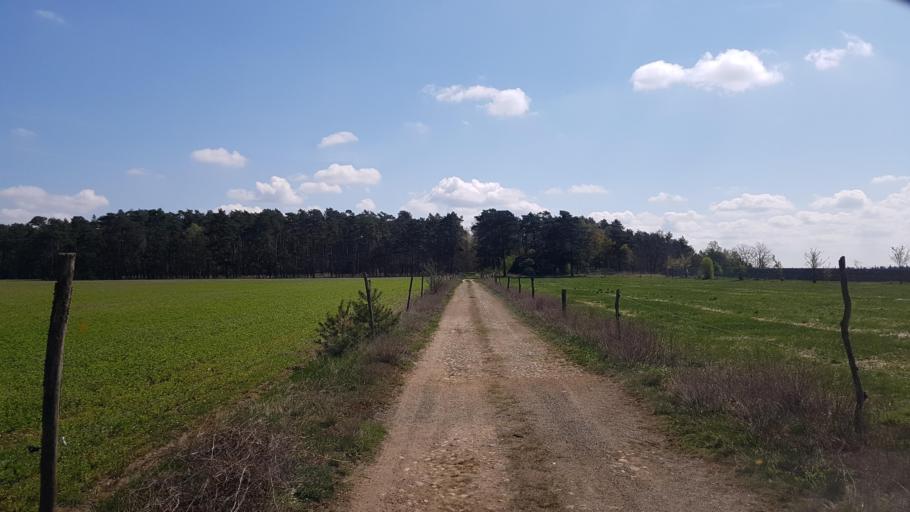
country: DE
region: Brandenburg
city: Bronkow
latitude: 51.6773
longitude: 13.9611
